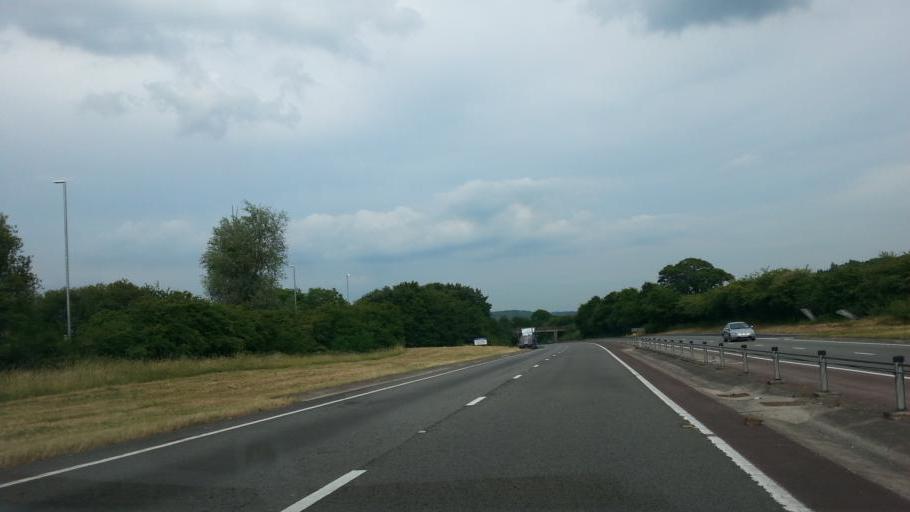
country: GB
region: Wales
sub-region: Monmouthshire
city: Mitchel Troy
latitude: 51.7728
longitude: -2.8123
